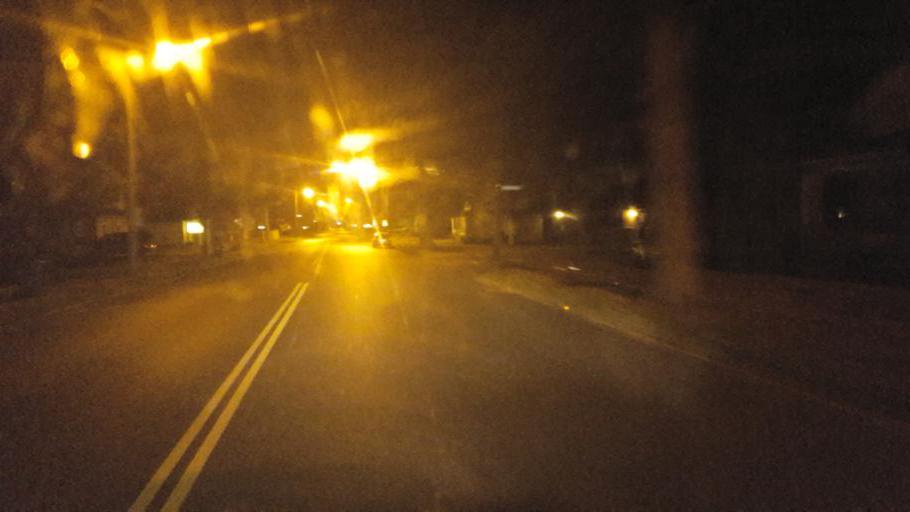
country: US
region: Ohio
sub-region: Knox County
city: Mount Vernon
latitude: 40.4039
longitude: -82.4921
